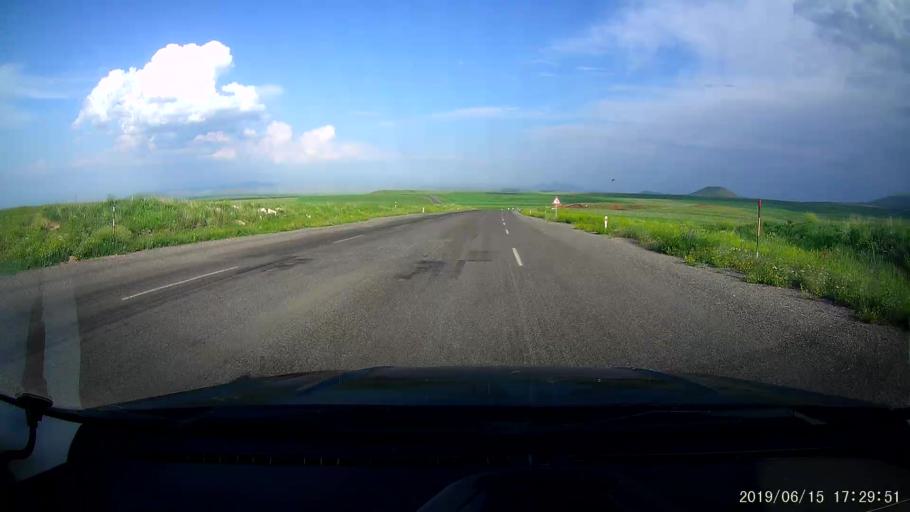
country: TR
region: Kars
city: Basgedikler
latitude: 40.5862
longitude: 43.4599
